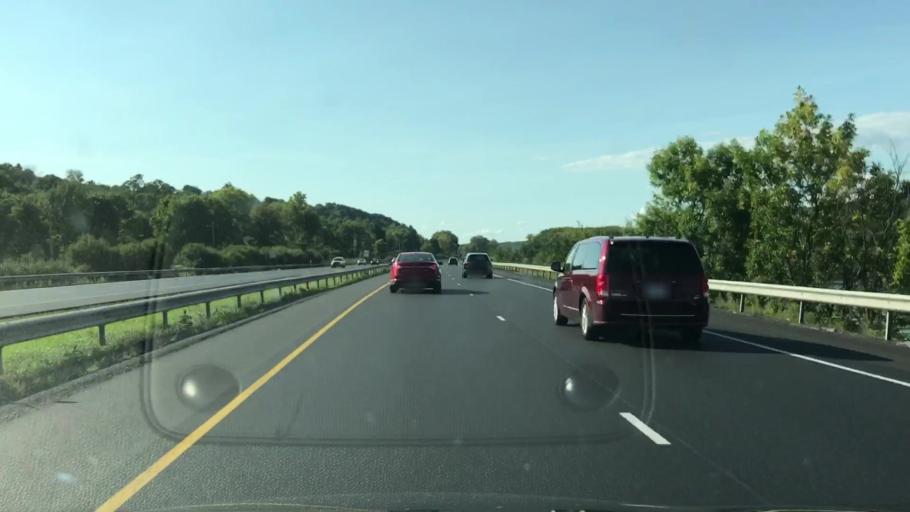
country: US
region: New York
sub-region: Montgomery County
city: Canajoharie
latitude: 42.8959
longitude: -74.5355
